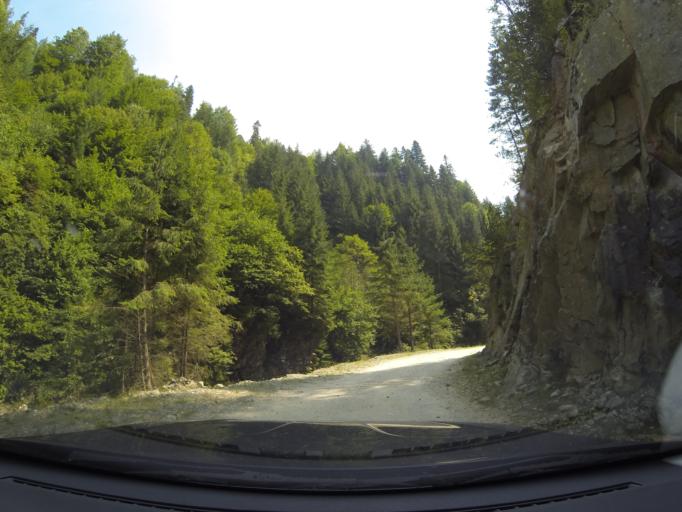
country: RO
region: Arges
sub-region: Comuna Arefu
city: Arefu
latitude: 45.4681
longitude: 24.6343
